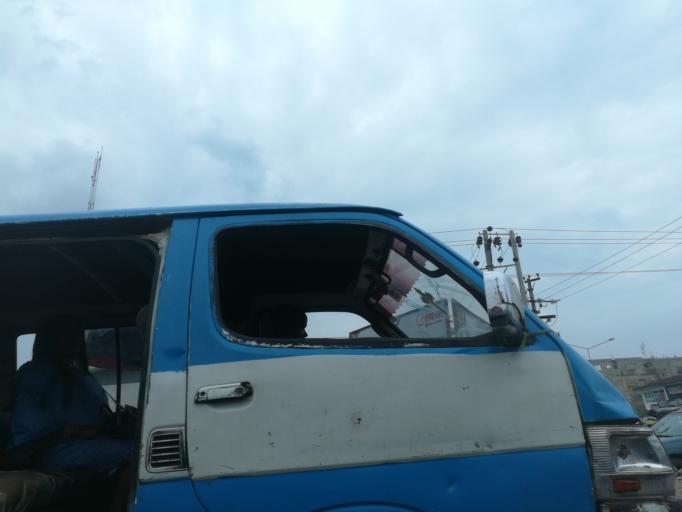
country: NG
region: Rivers
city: Port Harcourt
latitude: 4.8524
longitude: 6.9757
